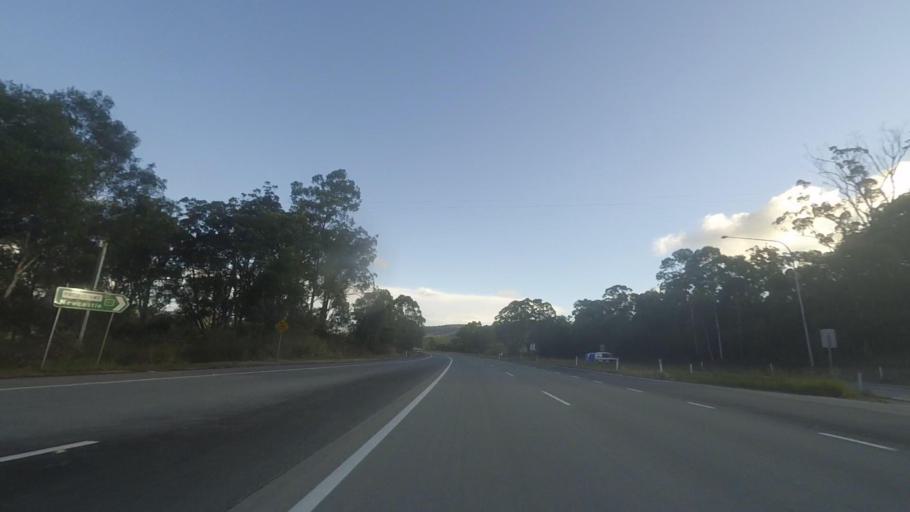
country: AU
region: New South Wales
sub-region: Great Lakes
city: Nabiac
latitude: -32.2523
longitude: 152.3234
